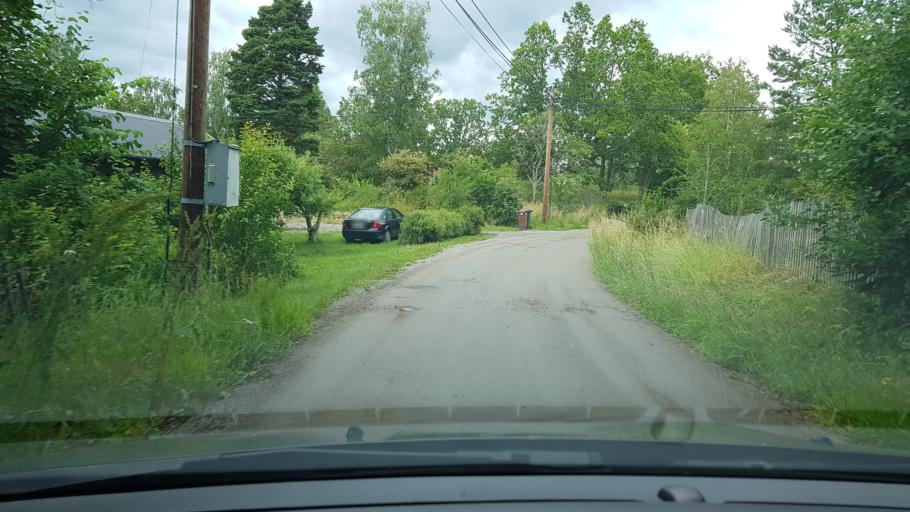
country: SE
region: Uppsala
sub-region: Uppsala Kommun
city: Alsike
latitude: 59.7173
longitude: 17.7011
